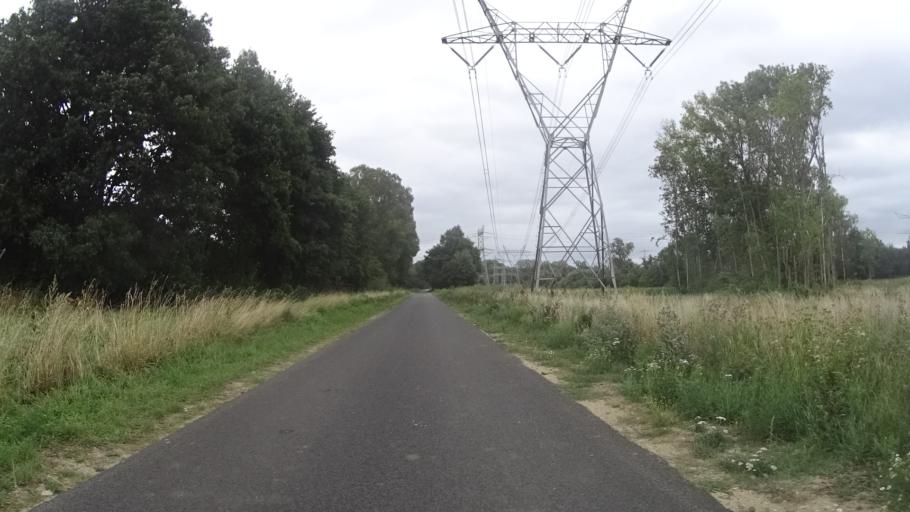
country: NL
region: Limburg
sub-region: Gemeente Maasgouw
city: Maasbracht
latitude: 51.1524
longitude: 5.9127
